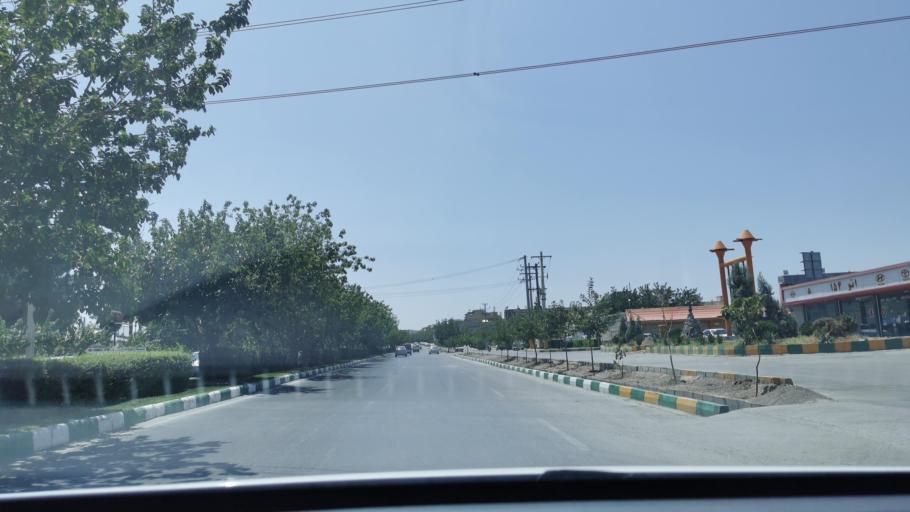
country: IR
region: Razavi Khorasan
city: Mashhad
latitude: 36.3501
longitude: 59.6292
